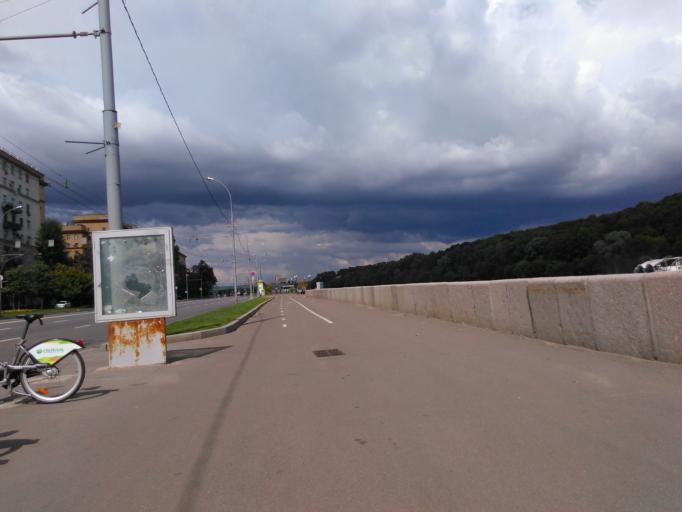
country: RU
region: Moscow
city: Novyye Cheremushki
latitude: 55.7155
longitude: 37.5780
